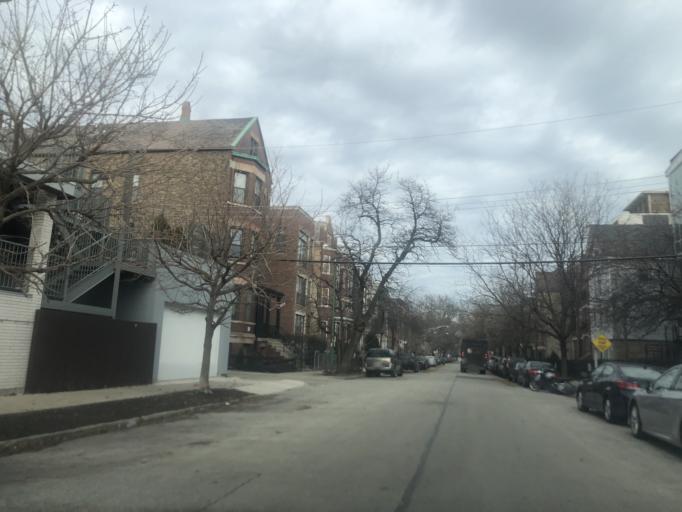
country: US
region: Illinois
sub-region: Cook County
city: Chicago
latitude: 41.8998
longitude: -87.6710
